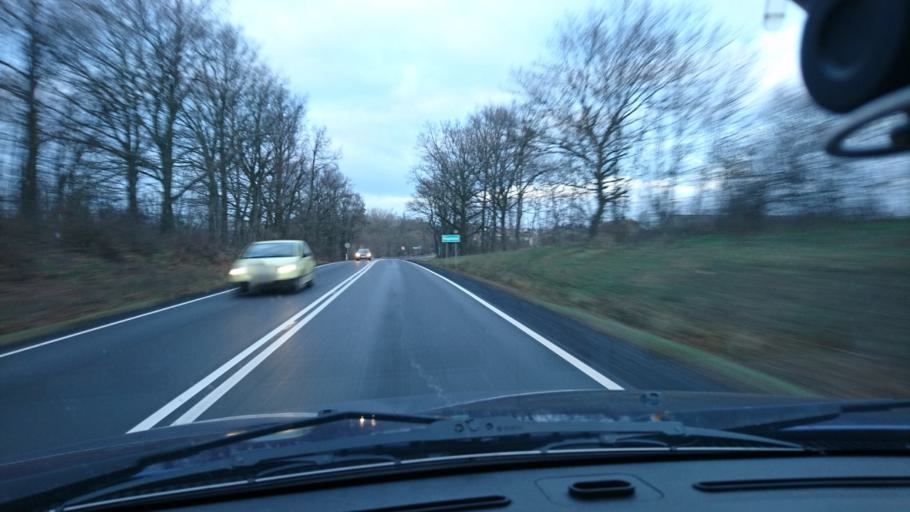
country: PL
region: Greater Poland Voivodeship
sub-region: Powiat ostrzeszowski
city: Ostrzeszow
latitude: 51.3793
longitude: 17.9458
